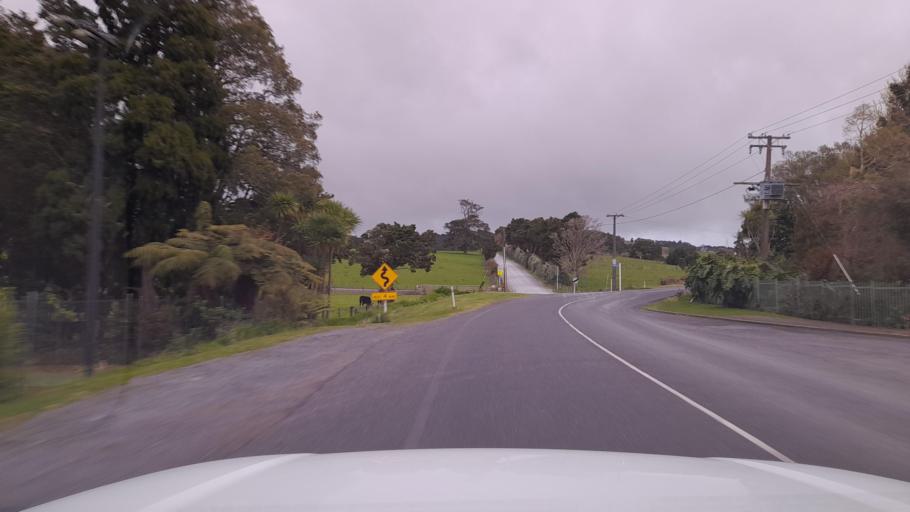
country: NZ
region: Northland
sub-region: Whangarei
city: Maungatapere
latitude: -35.6585
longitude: 174.2221
